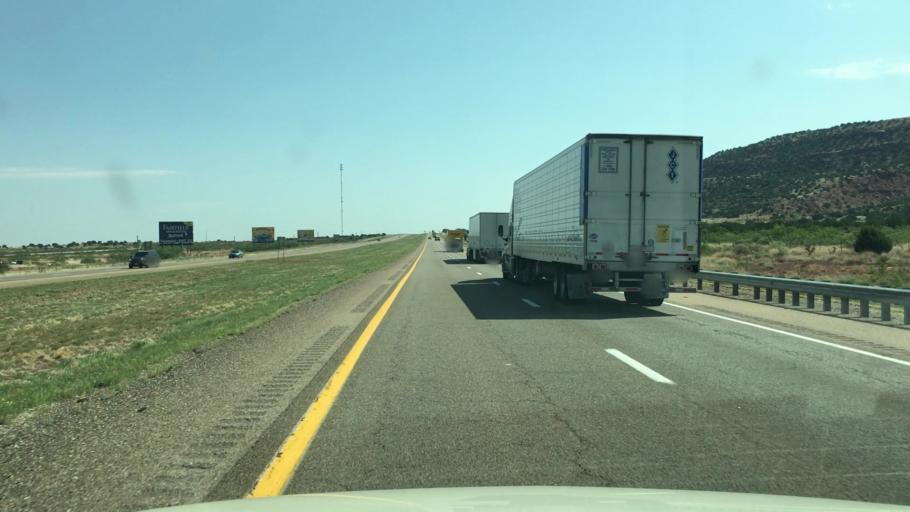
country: US
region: New Mexico
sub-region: Guadalupe County
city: Santa Rosa
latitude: 35.0396
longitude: -104.3913
